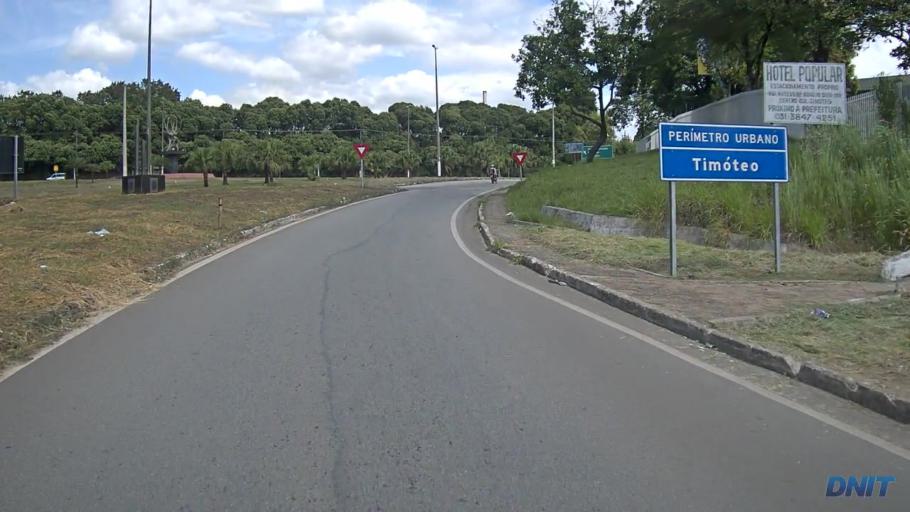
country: BR
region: Minas Gerais
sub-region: Coronel Fabriciano
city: Coronel Fabriciano
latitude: -19.5265
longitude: -42.6405
